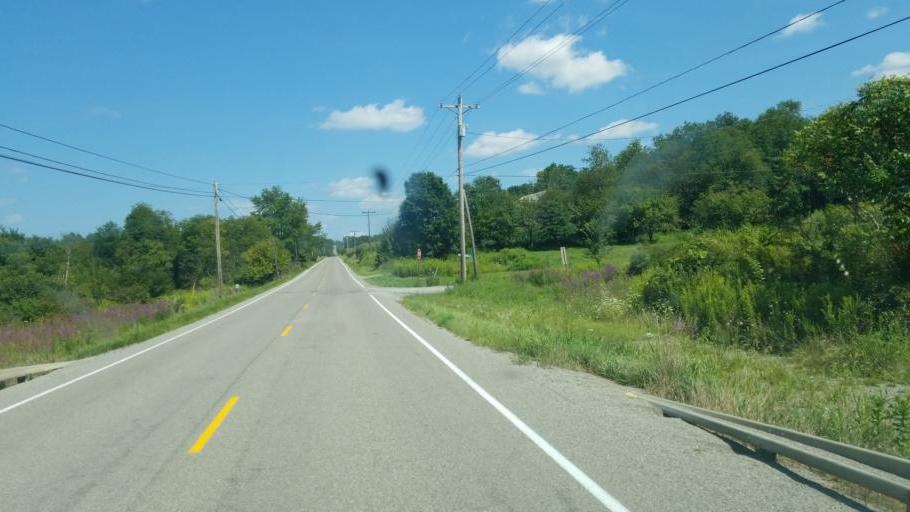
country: US
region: Pennsylvania
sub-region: Clarion County
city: Knox
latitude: 41.1021
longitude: -79.6525
